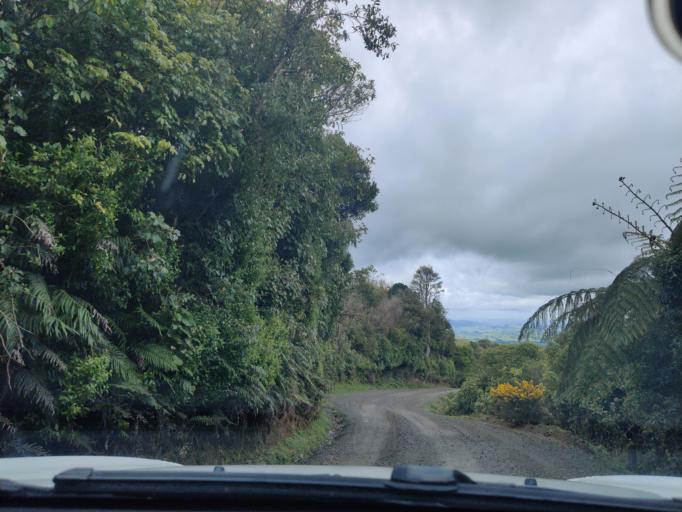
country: NZ
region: Manawatu-Wanganui
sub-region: Palmerston North City
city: Palmerston North
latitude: -40.2721
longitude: 175.8494
